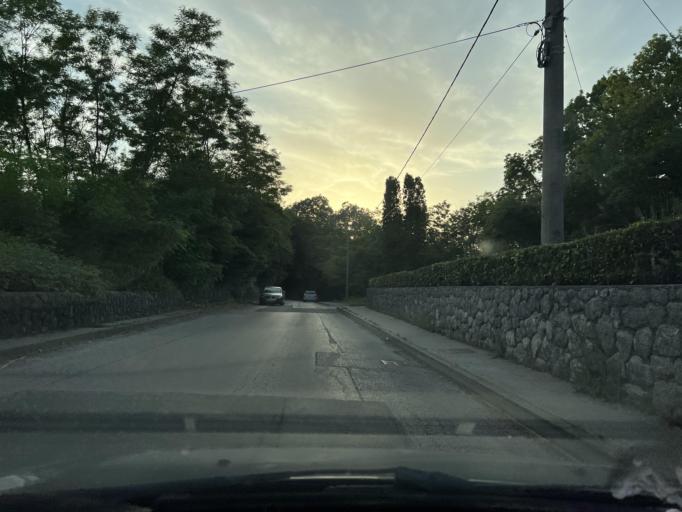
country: HR
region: Primorsko-Goranska
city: Drazice
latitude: 45.3892
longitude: 14.4407
